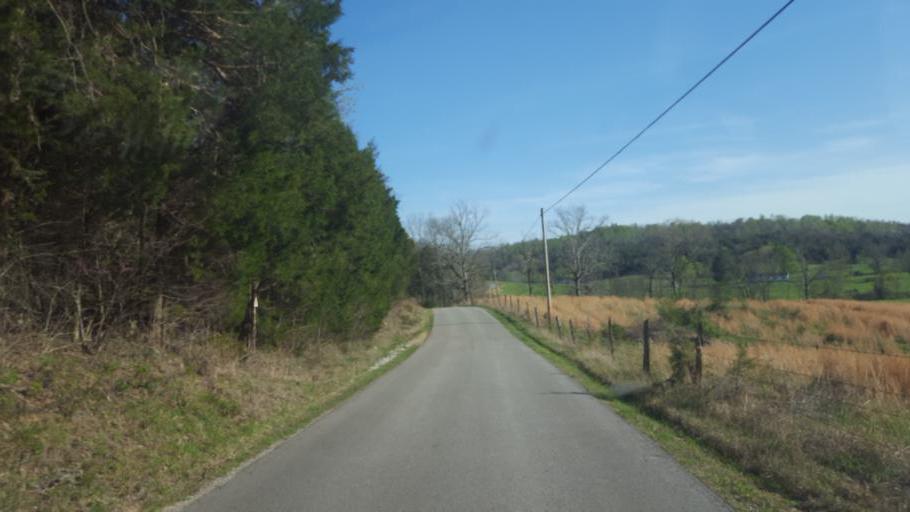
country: US
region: Kentucky
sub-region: Barren County
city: Cave City
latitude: 37.1850
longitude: -86.0111
